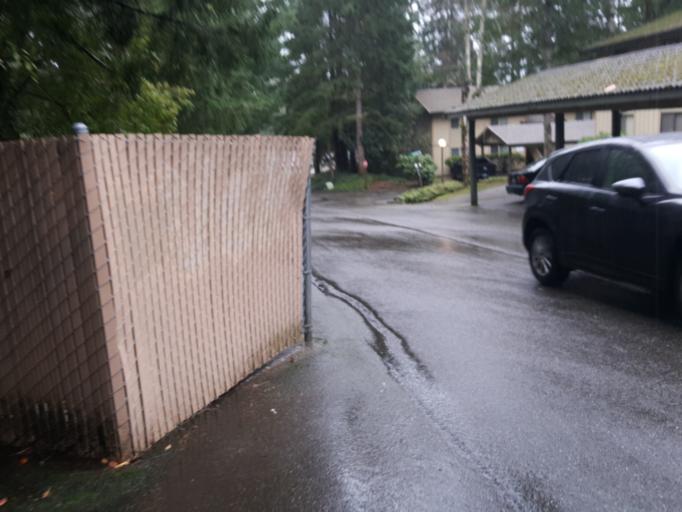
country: US
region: Washington
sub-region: Pierce County
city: University Place
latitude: 47.2062
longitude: -122.5359
